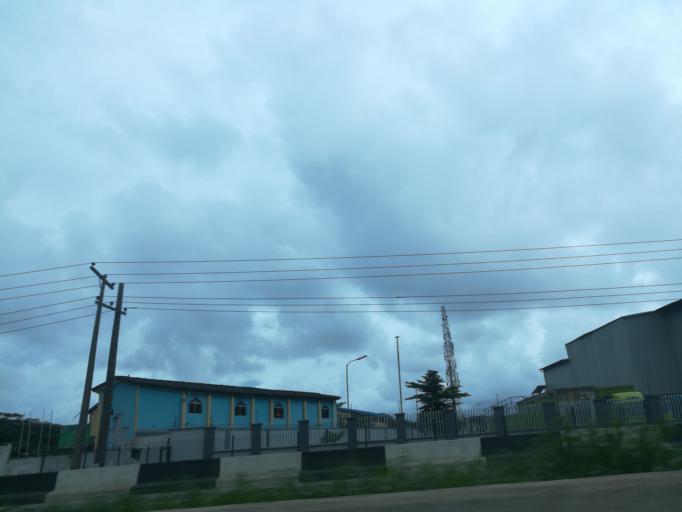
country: NG
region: Lagos
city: Lagos
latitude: 6.4584
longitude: 3.4034
